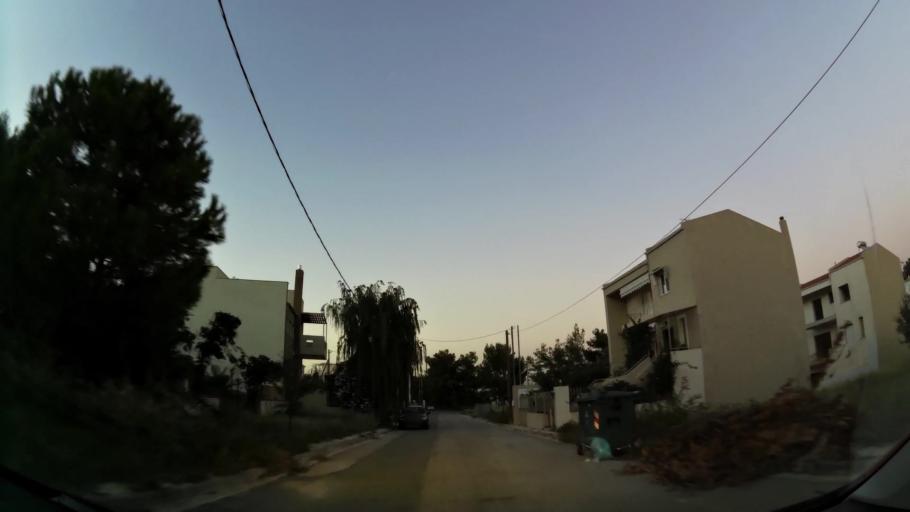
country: GR
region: Attica
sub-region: Nomarchia Anatolikis Attikis
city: Paiania
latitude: 37.9471
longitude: 23.8565
